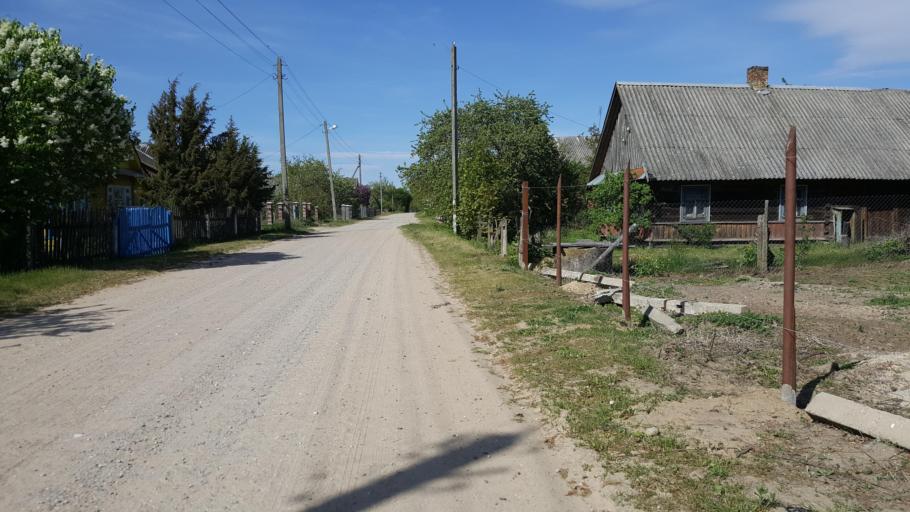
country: BY
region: Brest
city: Zhabinka
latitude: 52.3193
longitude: 24.0431
